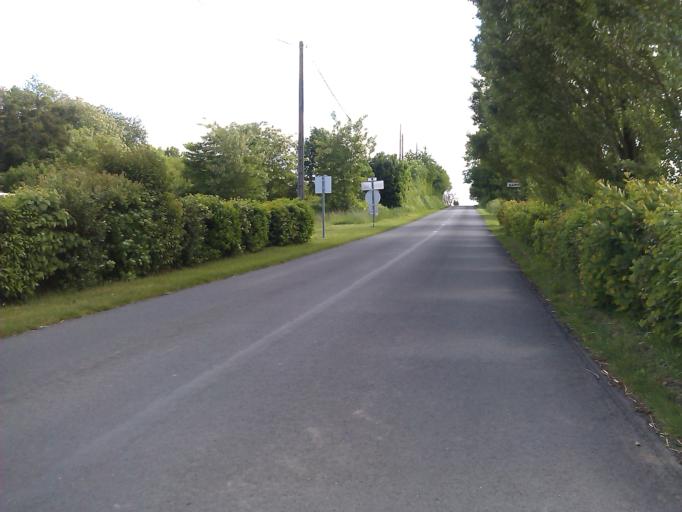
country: FR
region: Poitou-Charentes
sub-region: Departement de la Charente
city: Mansle
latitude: 45.8701
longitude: 0.1743
